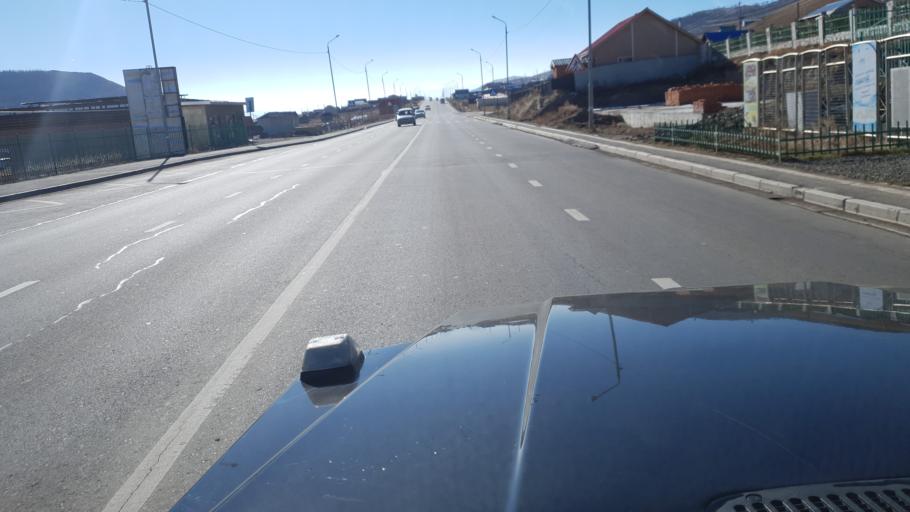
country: MN
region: Ulaanbaatar
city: Ulaanbaatar
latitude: 48.0442
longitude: 106.9026
